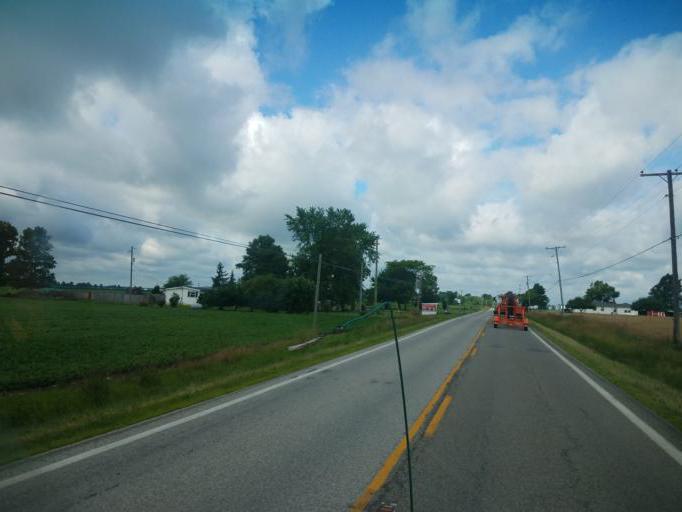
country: US
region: Ohio
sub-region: Marion County
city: Prospect
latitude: 40.4414
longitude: -83.2341
